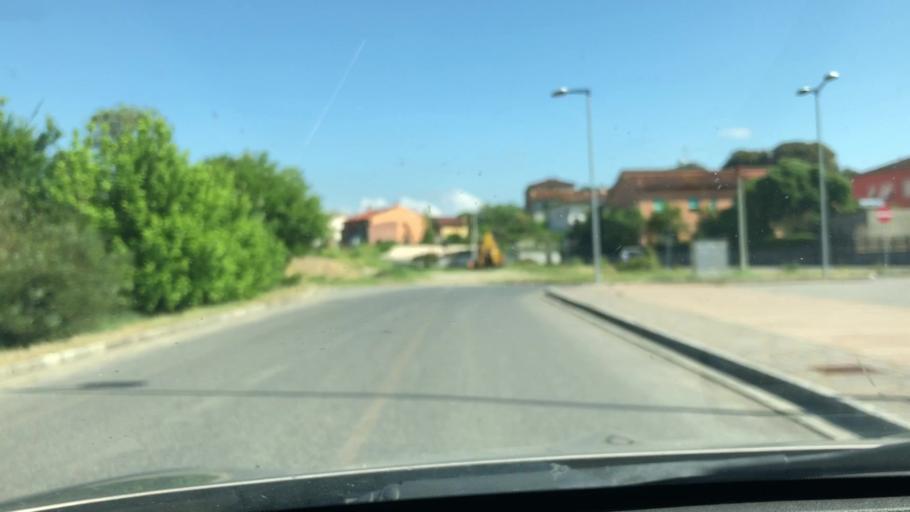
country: IT
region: Tuscany
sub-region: Province of Pisa
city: Capannoli
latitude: 43.5885
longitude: 10.6756
